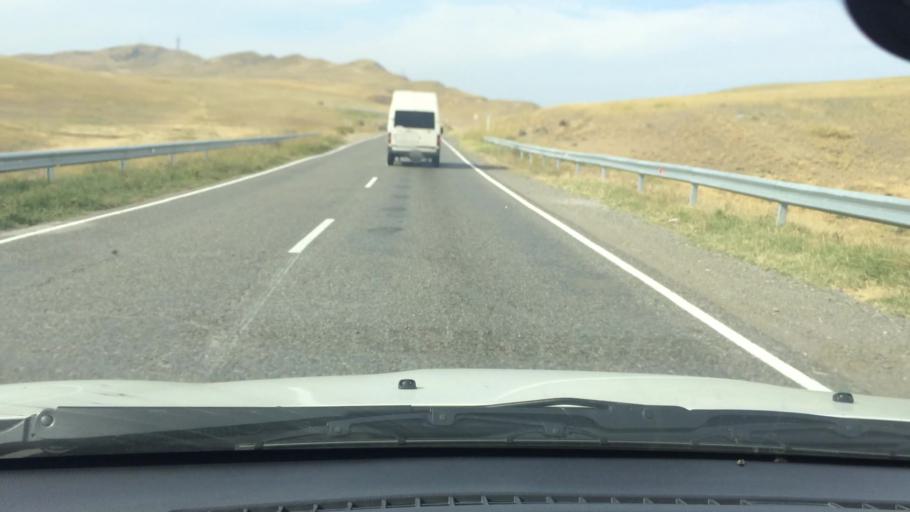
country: GE
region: Kvemo Kartli
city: Rust'avi
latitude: 41.5301
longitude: 44.9786
